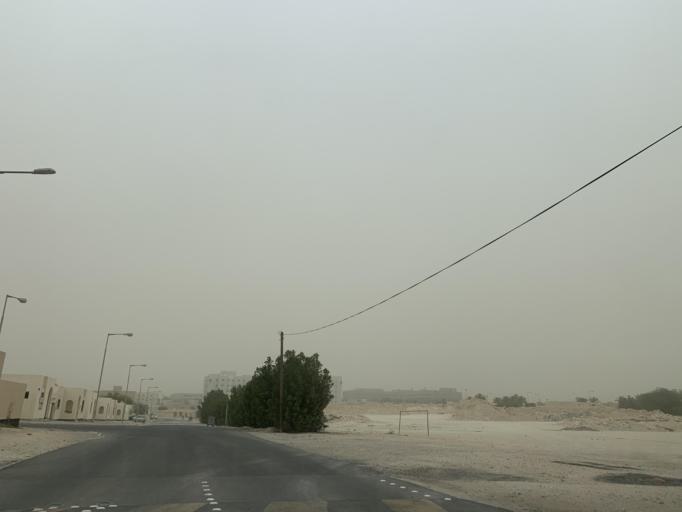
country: BH
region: Central Governorate
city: Madinat Hamad
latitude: 26.1308
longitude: 50.5210
